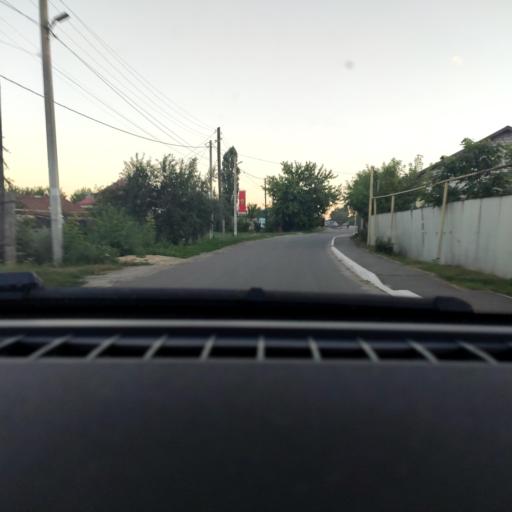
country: RU
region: Voronezj
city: Novaya Usman'
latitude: 51.6606
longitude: 39.3416
